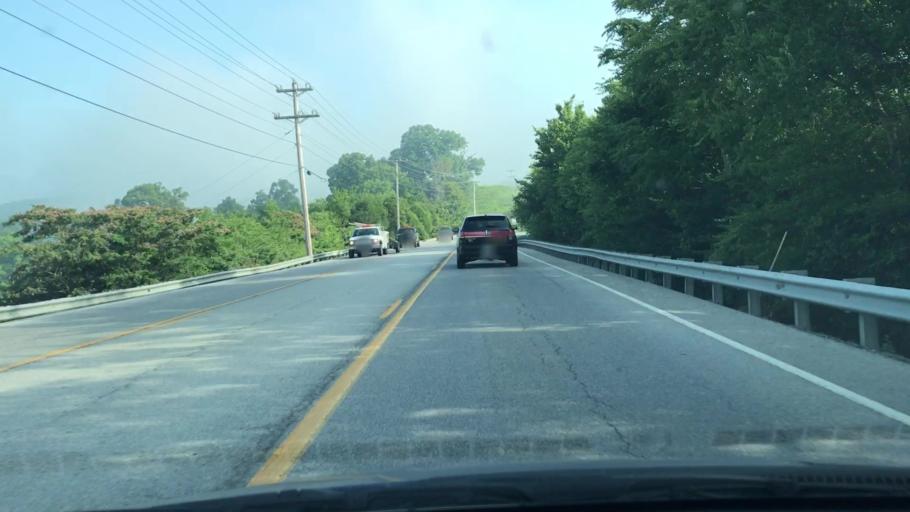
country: US
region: Tennessee
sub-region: Smith County
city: South Carthage
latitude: 36.2133
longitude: -85.9533
